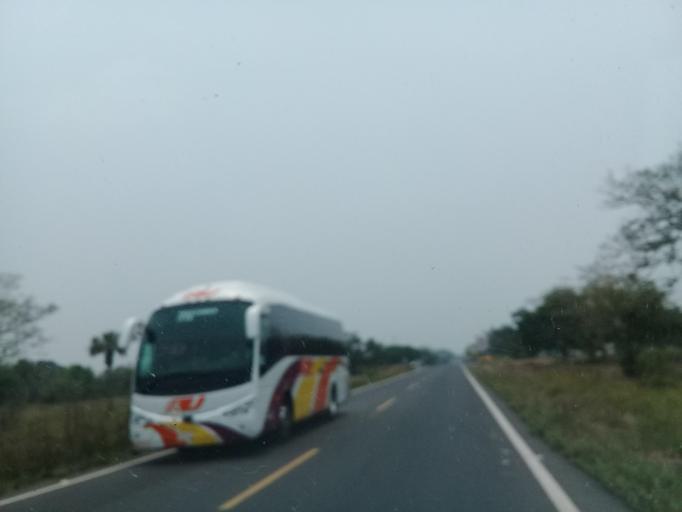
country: MX
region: Veracruz
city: Paso del Toro
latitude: 18.9799
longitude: -96.1753
